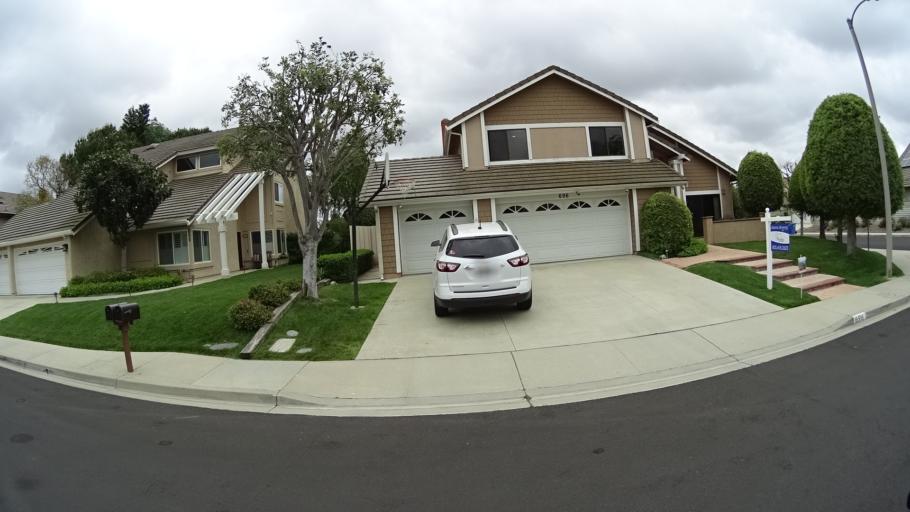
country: US
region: California
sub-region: Ventura County
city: Casa Conejo
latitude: 34.2231
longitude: -118.8941
